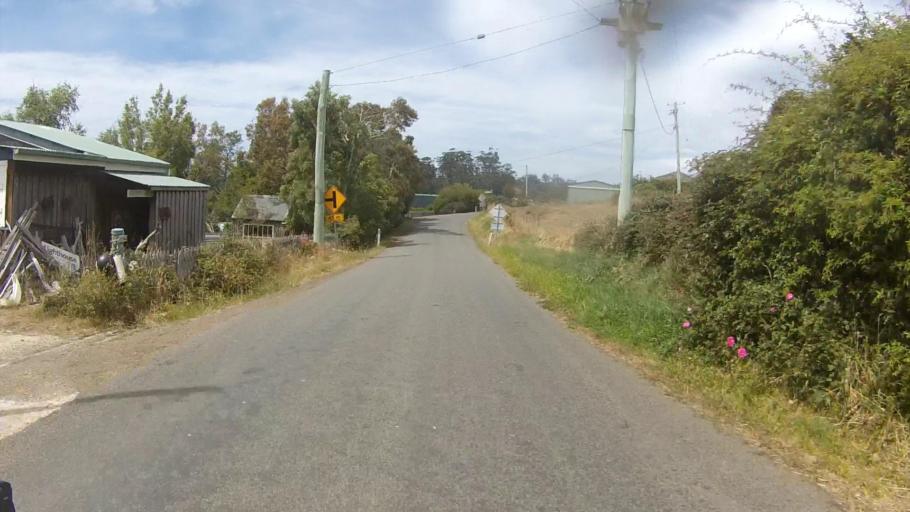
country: AU
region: Tasmania
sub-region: Sorell
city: Sorell
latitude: -42.8081
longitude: 147.8324
